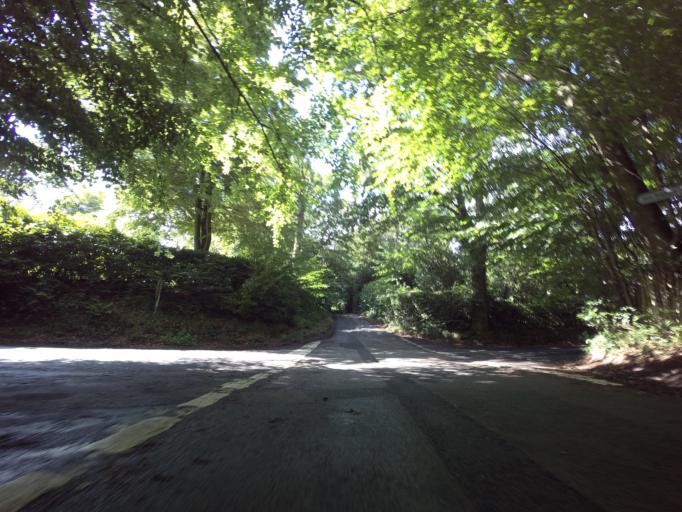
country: GB
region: England
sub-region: Kent
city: Borough Green
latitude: 51.2731
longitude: 0.2781
